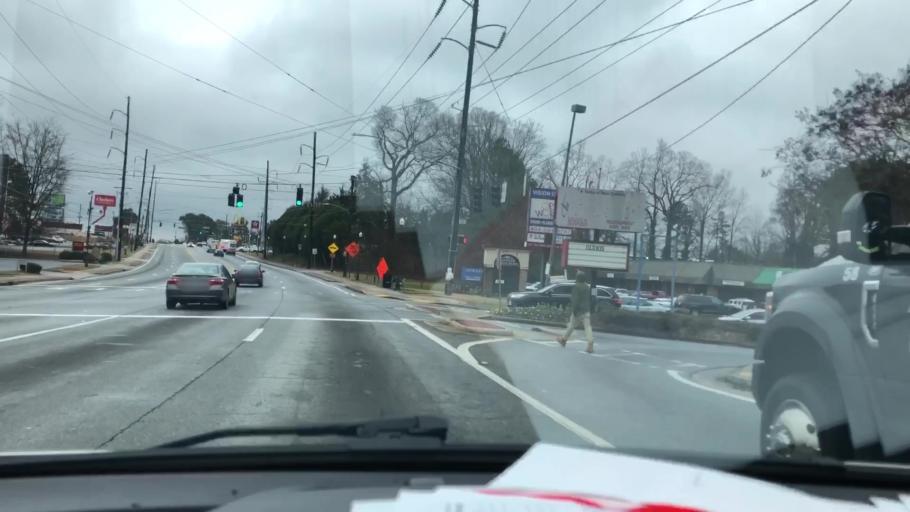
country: US
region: Georgia
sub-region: DeKalb County
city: Panthersville
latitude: 33.7072
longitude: -84.2722
